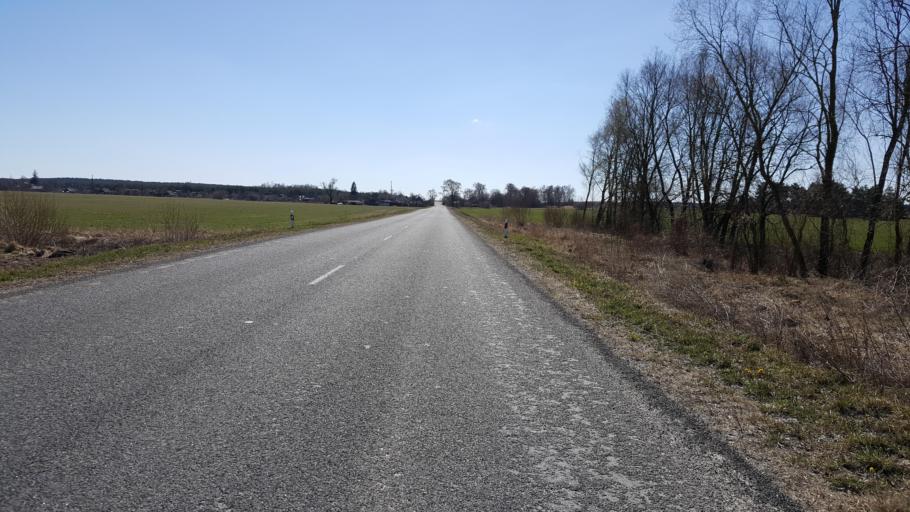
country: BY
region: Brest
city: Charnawchytsy
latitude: 52.2663
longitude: 23.8517
